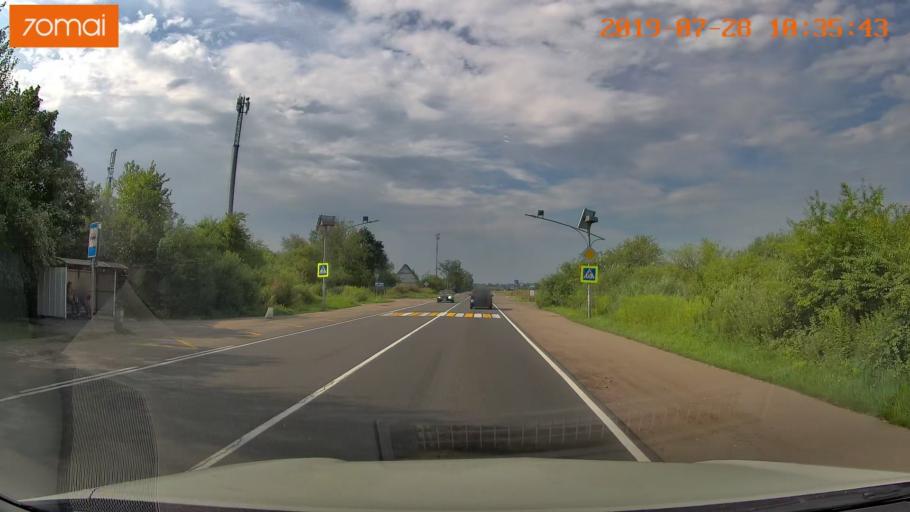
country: RU
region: Kaliningrad
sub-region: Gorod Kaliningrad
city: Kaliningrad
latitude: 54.7441
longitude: 20.4289
